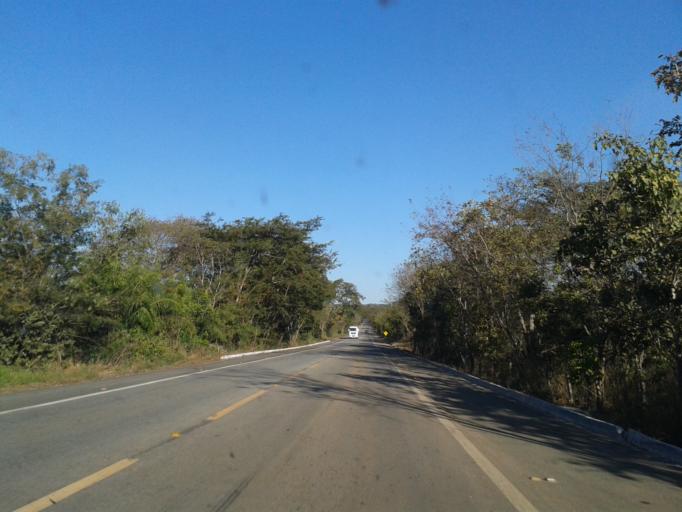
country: BR
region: Goias
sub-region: Itapuranga
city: Itapuranga
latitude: -15.3414
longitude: -50.4126
